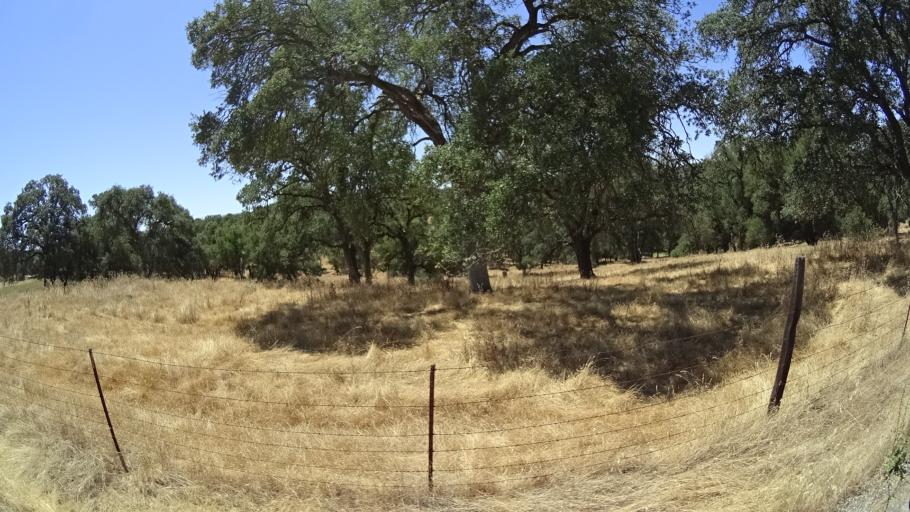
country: US
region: California
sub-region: Calaveras County
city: Angels Camp
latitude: 38.1097
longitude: -120.6106
